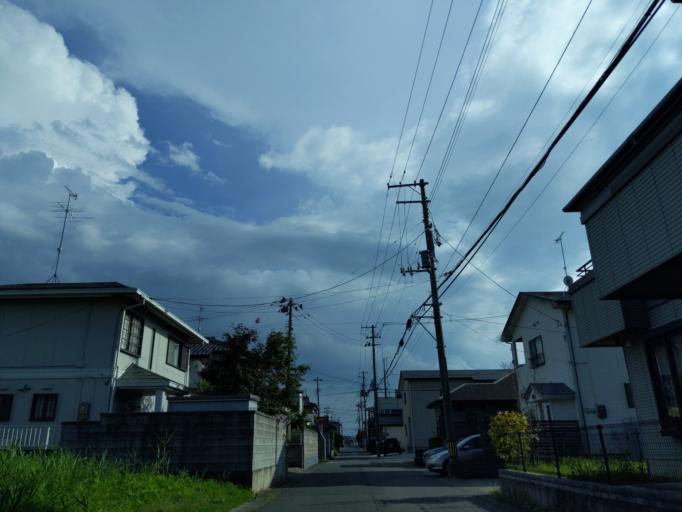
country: JP
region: Fukushima
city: Koriyama
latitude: 37.3885
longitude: 140.3300
